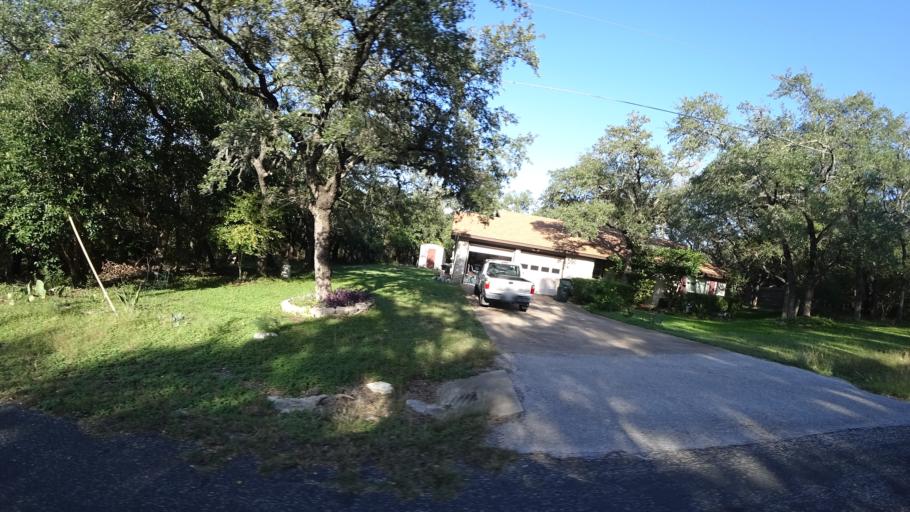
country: US
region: Texas
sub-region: Travis County
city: Barton Creek
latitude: 30.2418
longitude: -97.9145
